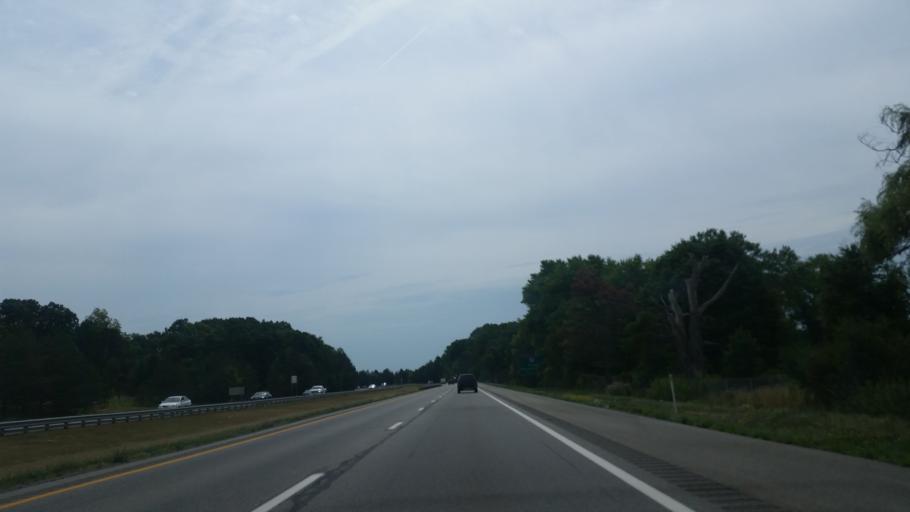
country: US
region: Ohio
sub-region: Cuyahoga County
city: Solon
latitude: 41.3972
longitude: -81.4518
